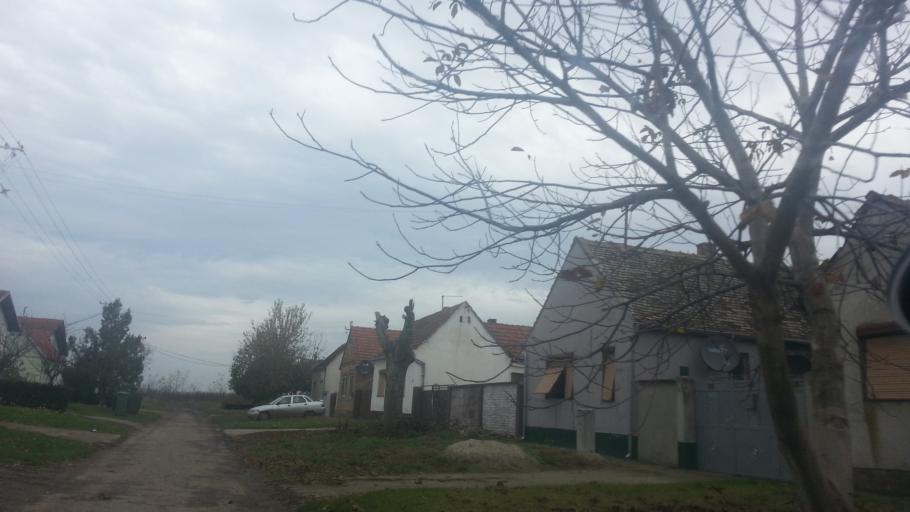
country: RS
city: Golubinci
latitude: 44.9971
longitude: 20.0650
